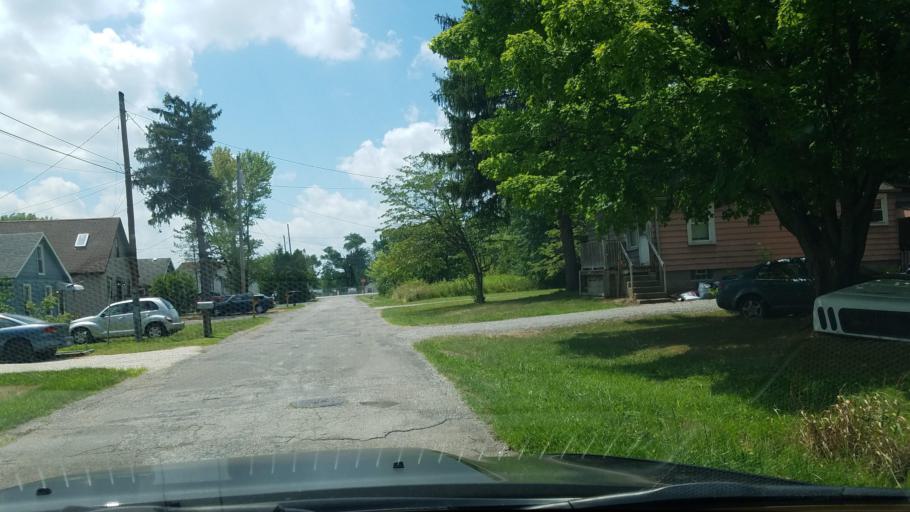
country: US
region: Ohio
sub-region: Trumbull County
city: Bolindale
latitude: 41.2022
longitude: -80.7766
